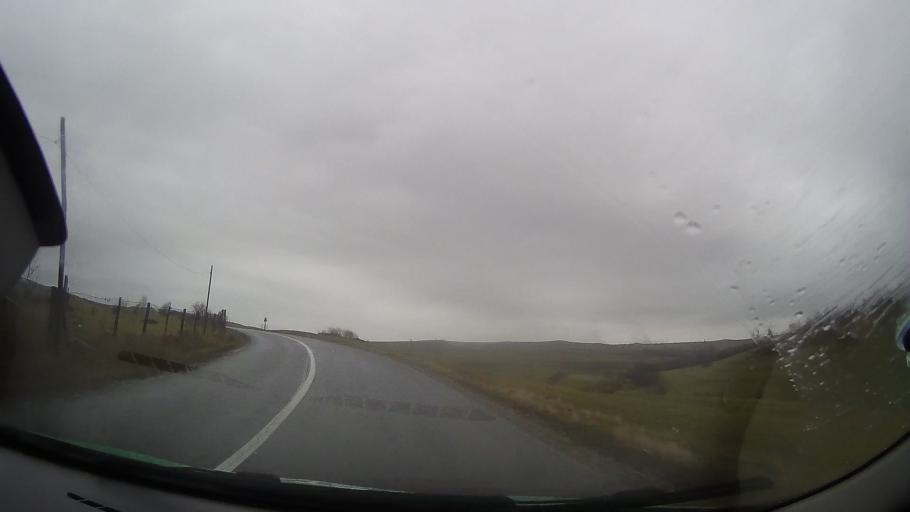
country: RO
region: Bistrita-Nasaud
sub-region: Comuna Monor
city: Monor
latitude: 46.9533
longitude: 24.6804
